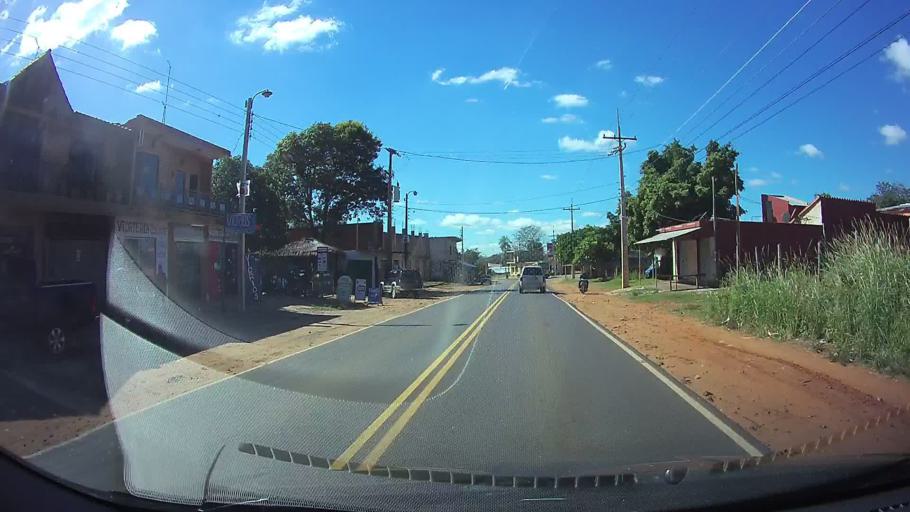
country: PY
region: Central
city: Limpio
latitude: -25.2117
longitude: -57.4665
